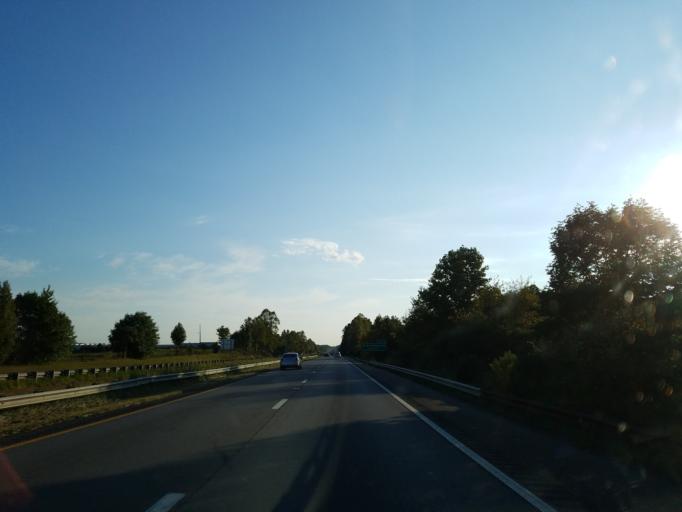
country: US
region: North Carolina
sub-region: Cleveland County
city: Kings Mountain
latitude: 35.2217
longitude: -81.3390
